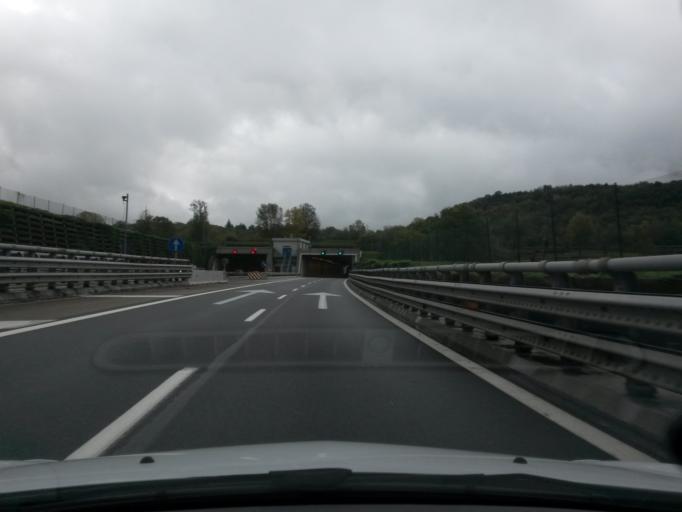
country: IT
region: Piedmont
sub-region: Provincia di Torino
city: Caselette
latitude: 45.0865
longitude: 7.4875
